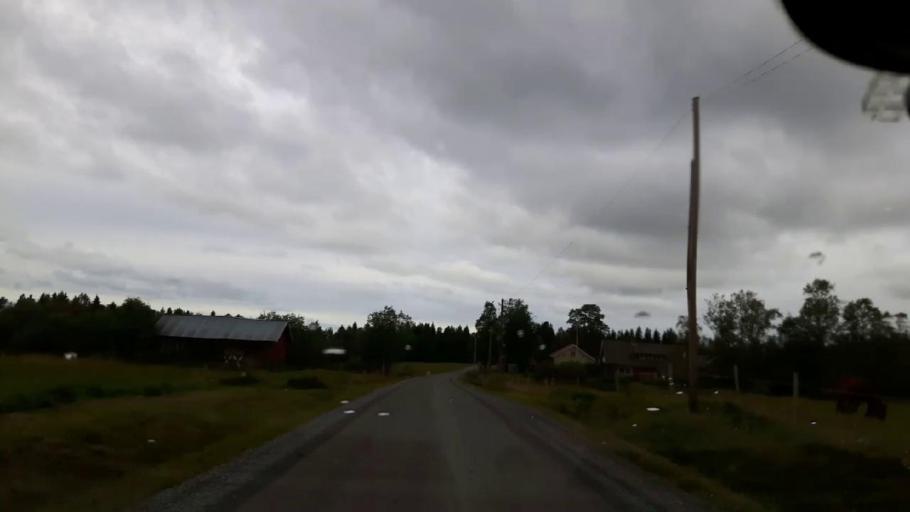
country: SE
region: Jaemtland
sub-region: OEstersunds Kommun
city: Ostersund
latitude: 63.0572
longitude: 14.5589
